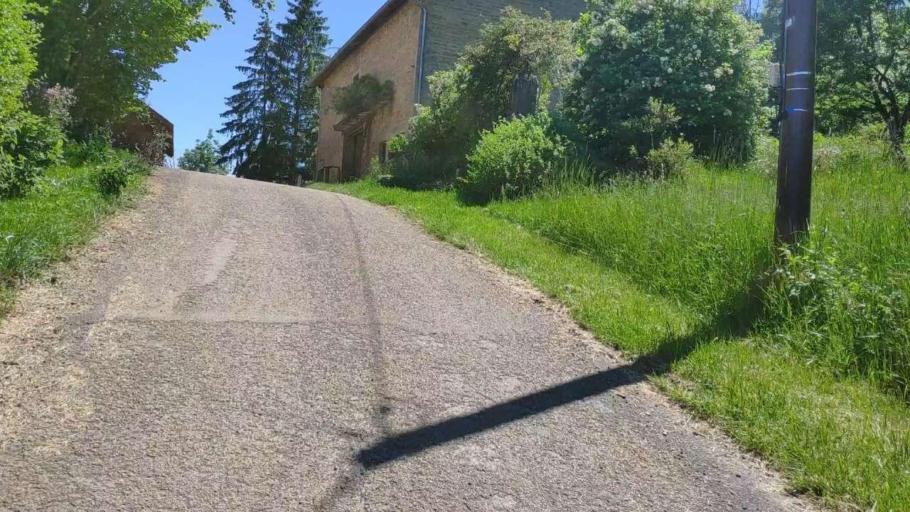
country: FR
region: Franche-Comte
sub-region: Departement du Jura
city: Perrigny
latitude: 46.7307
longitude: 5.6295
